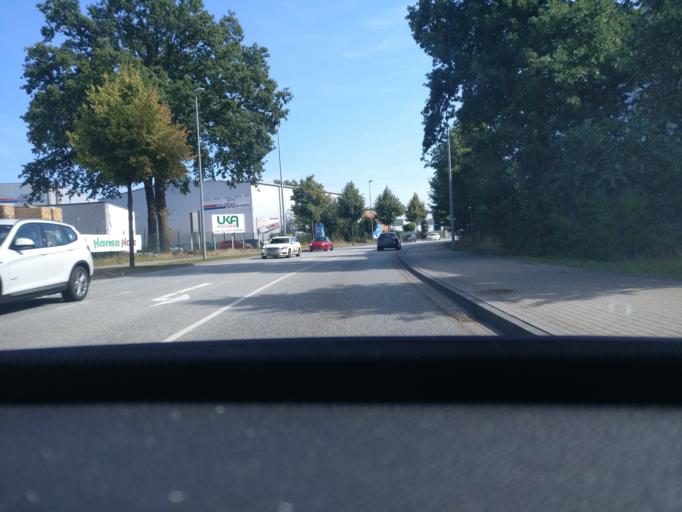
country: DE
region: Hamburg
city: Langenhorn
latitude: 53.6614
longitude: 9.9797
